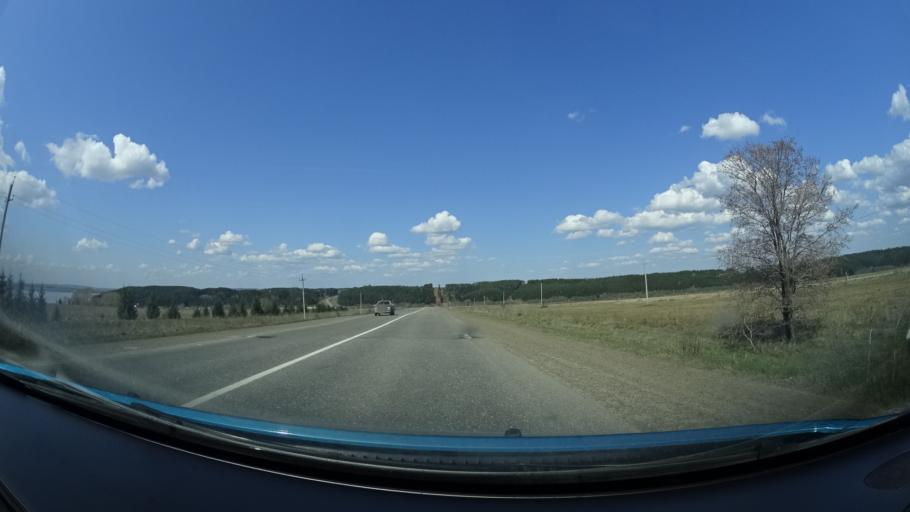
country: RU
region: Perm
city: Osa
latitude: 57.2471
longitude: 55.5908
